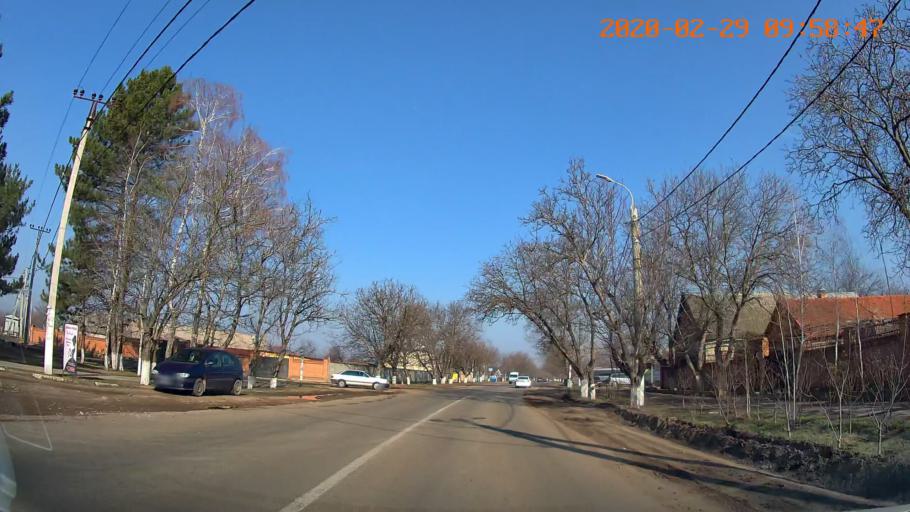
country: MD
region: Telenesti
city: Slobozia
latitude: 46.7516
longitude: 29.6897
